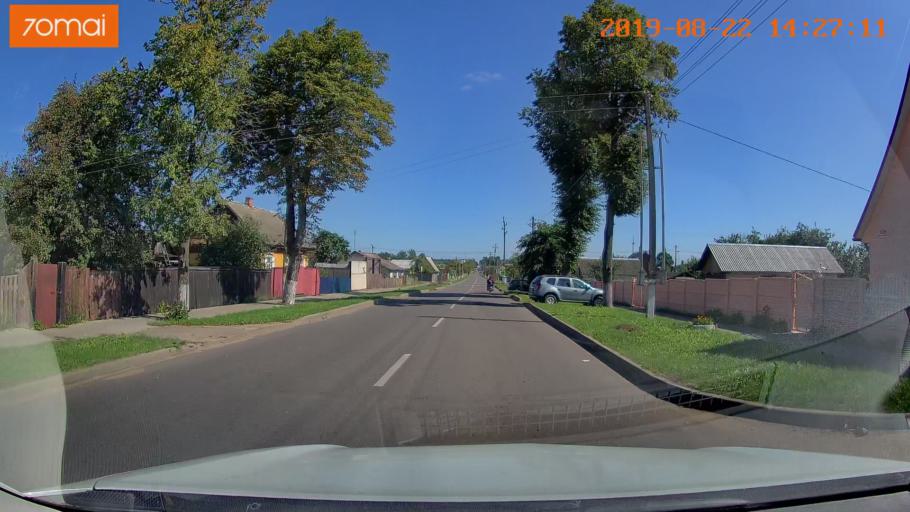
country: BY
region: Mogilev
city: Asipovichy
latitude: 53.2975
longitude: 28.6231
